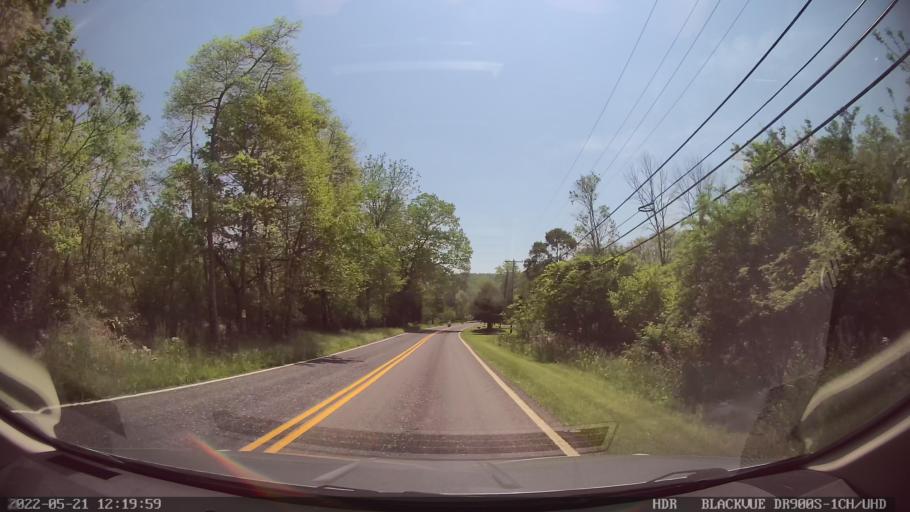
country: US
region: Pennsylvania
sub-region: Berks County
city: Bally
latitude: 40.4174
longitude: -75.6192
